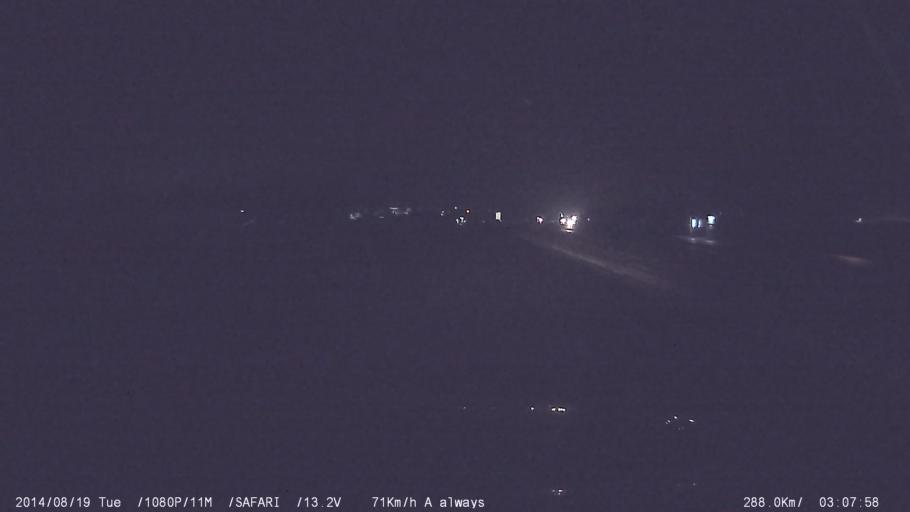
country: IN
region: Tamil Nadu
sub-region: Coimbatore
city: Sulur
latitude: 11.0872
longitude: 77.1294
